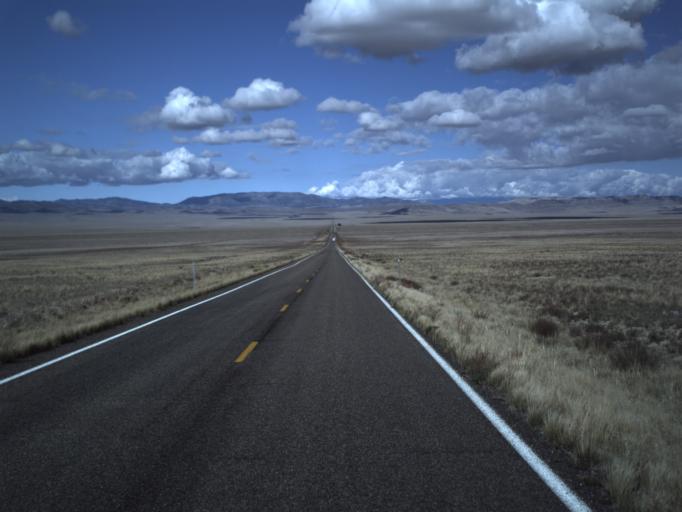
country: US
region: Utah
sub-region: Beaver County
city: Milford
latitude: 38.5163
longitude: -113.6385
